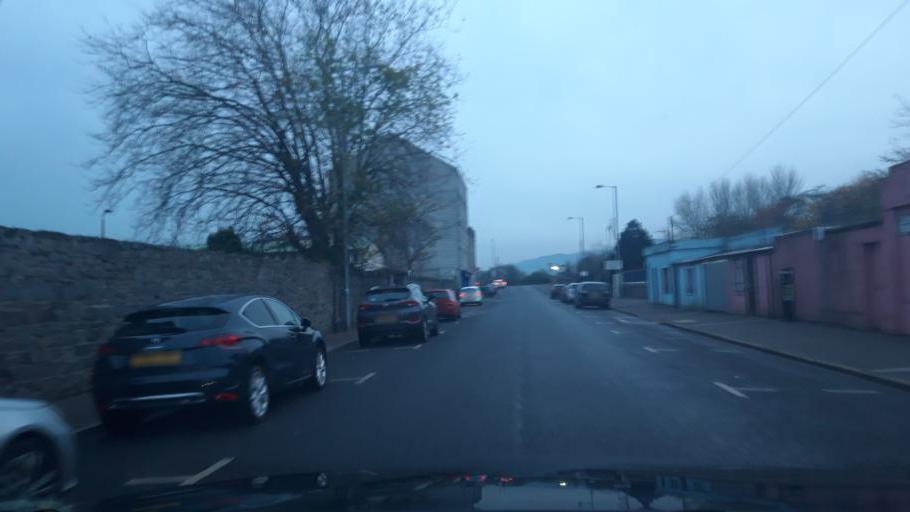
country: GB
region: Northern Ireland
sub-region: Newry and Mourne District
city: Newry
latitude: 54.1724
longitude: -6.3391
